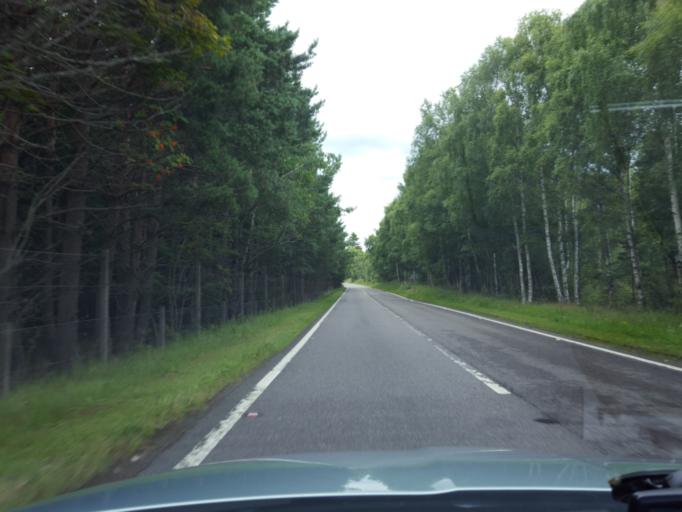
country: GB
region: Scotland
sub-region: Highland
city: Grantown on Spey
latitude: 57.3833
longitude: -3.4656
